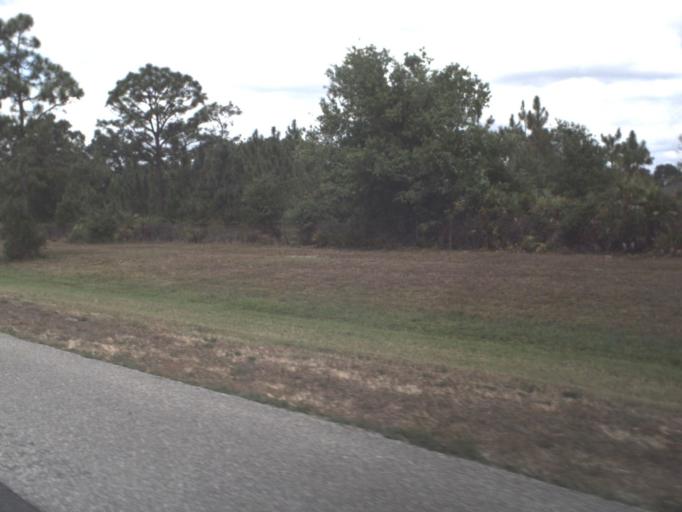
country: US
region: Florida
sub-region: Orange County
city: Wedgefield
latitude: 28.4519
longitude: -81.0839
